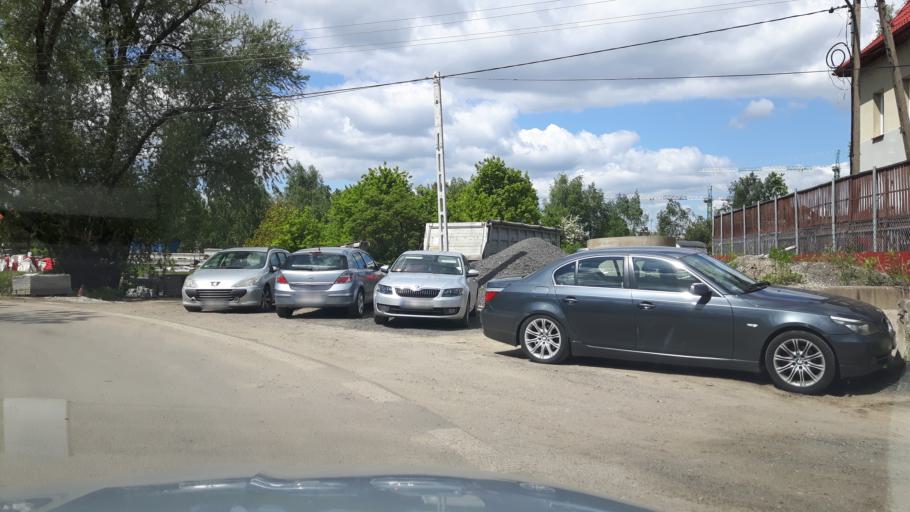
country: PL
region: Masovian Voivodeship
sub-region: Powiat legionowski
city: Stanislawow Pierwszy
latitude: 52.3404
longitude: 21.0400
